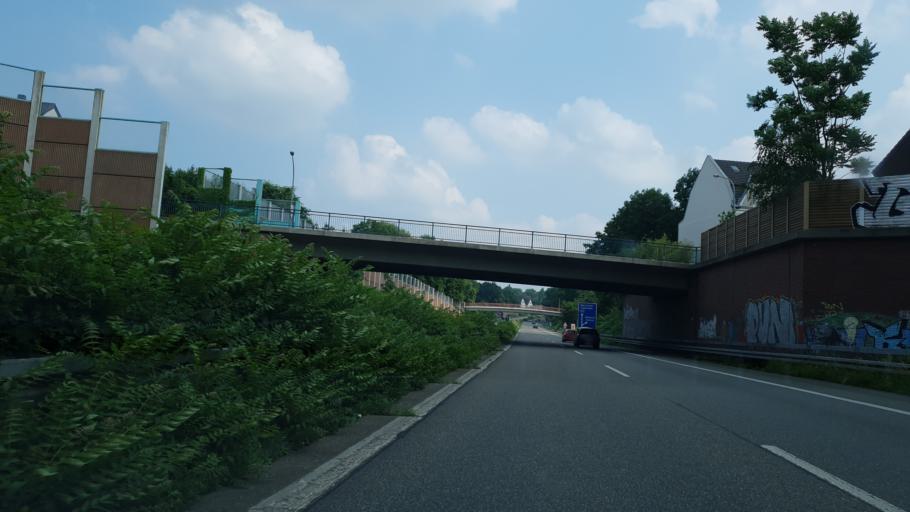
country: DE
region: North Rhine-Westphalia
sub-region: Regierungsbezirk Dusseldorf
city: Oberhausen
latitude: 51.5258
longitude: 6.8497
